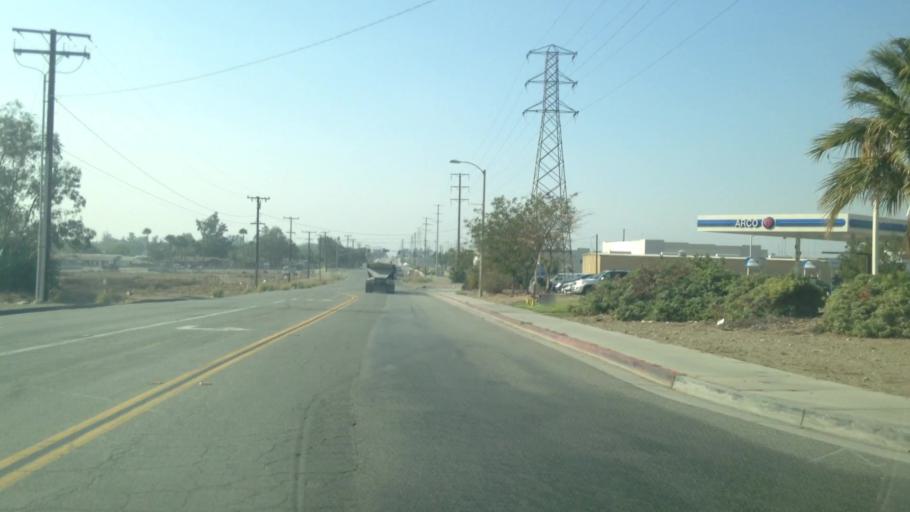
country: US
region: California
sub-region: Riverside County
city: Mira Loma
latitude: 34.0061
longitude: -117.5032
